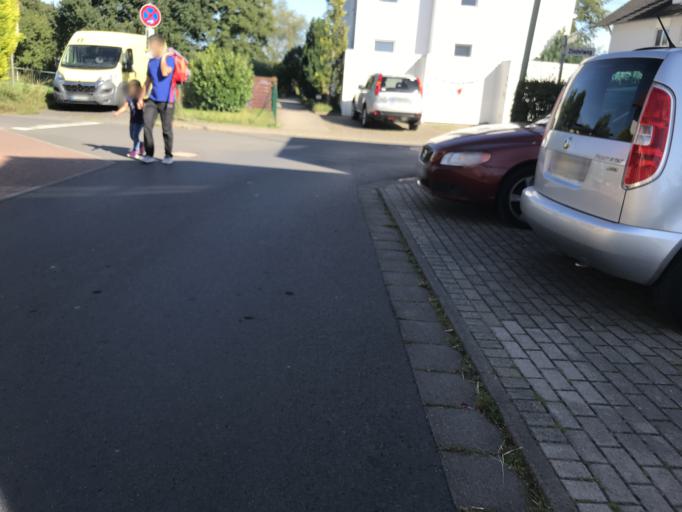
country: DE
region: Hesse
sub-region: Regierungsbezirk Darmstadt
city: Glauburg
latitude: 50.2931
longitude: 8.9838
